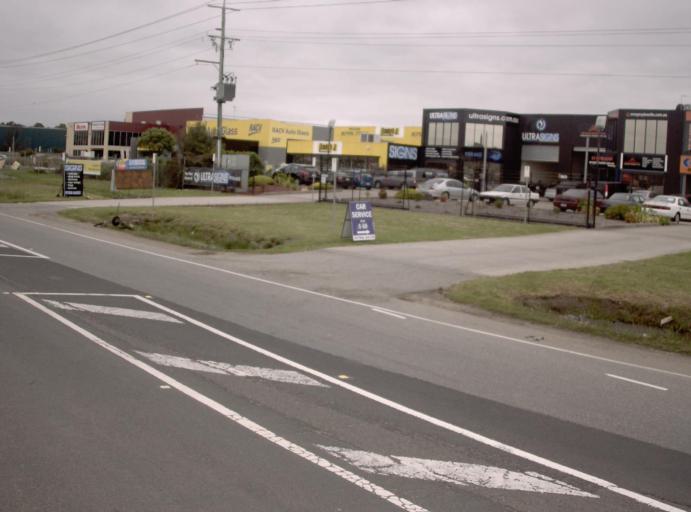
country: AU
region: Victoria
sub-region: Casey
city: Hallam
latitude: -38.0193
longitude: 145.2705
